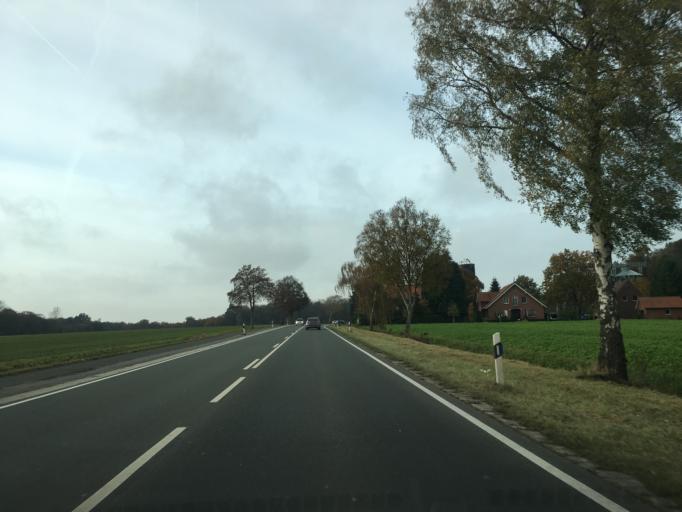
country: DE
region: North Rhine-Westphalia
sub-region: Regierungsbezirk Munster
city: Steinfurt
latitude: 52.1334
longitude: 7.3775
